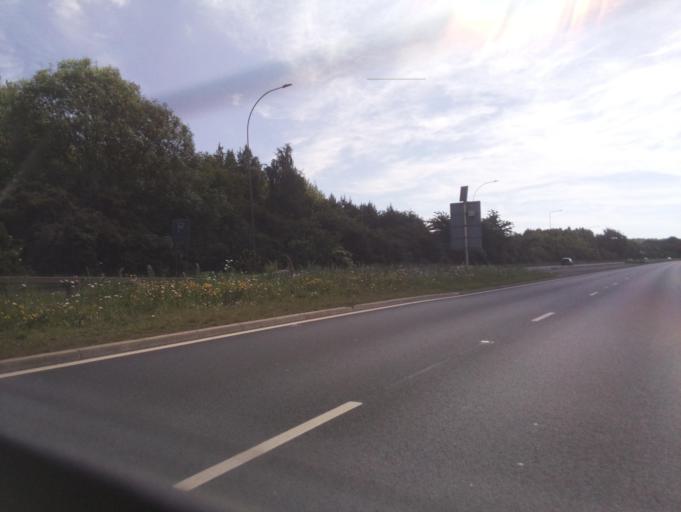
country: GB
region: England
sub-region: North Lincolnshire
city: Manton
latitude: 53.5628
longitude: -0.6026
